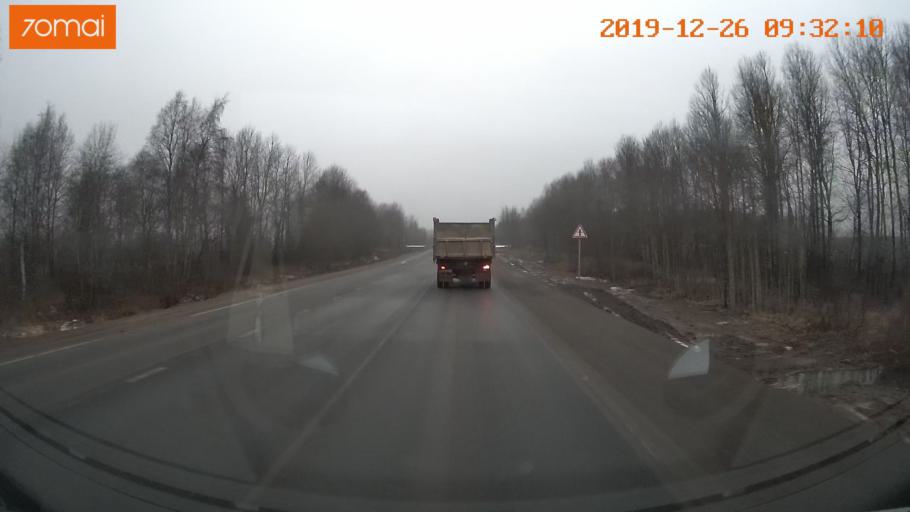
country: RU
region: Vologda
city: Gryazovets
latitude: 59.0753
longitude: 40.1199
